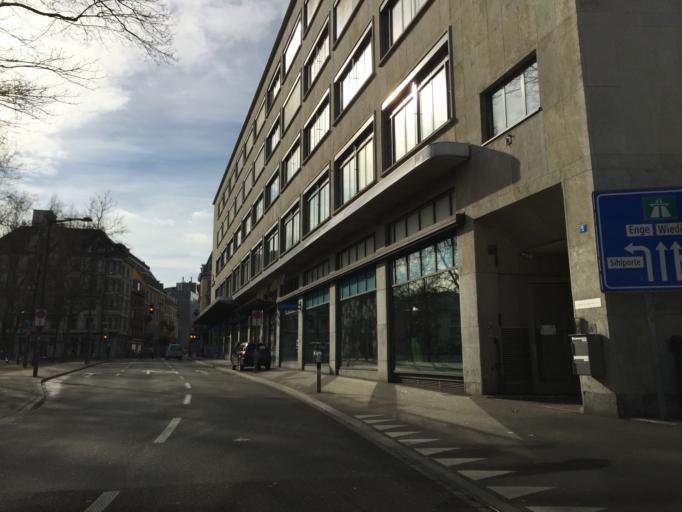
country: CH
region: Zurich
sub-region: Bezirk Zuerich
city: Zuerich (Kreis 1) / City
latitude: 47.3739
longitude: 8.5334
